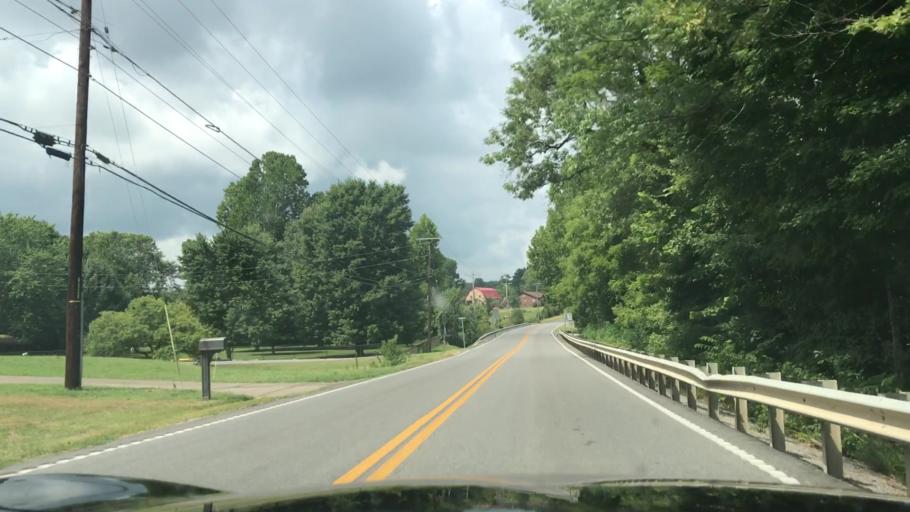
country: US
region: Kentucky
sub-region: Muhlenberg County
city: Greenville
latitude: 37.2052
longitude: -87.1611
